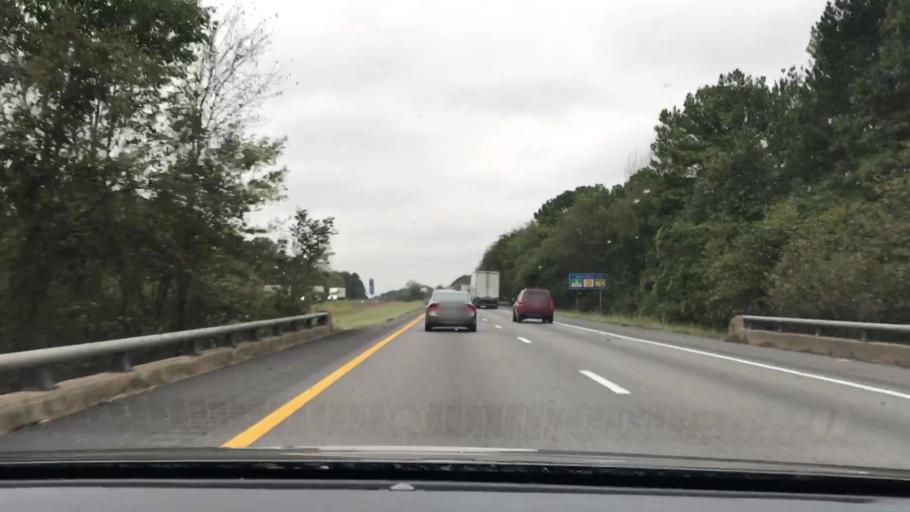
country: US
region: Tennessee
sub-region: Robertson County
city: Cross Plains
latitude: 36.5465
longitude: -86.6347
